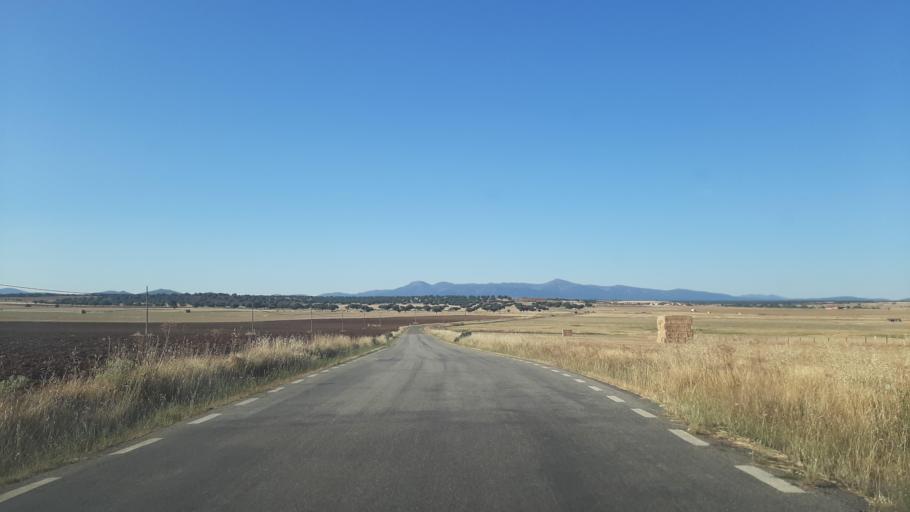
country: ES
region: Castille and Leon
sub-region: Provincia de Salamanca
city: Cabrillas
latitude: 40.7241
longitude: -6.1762
